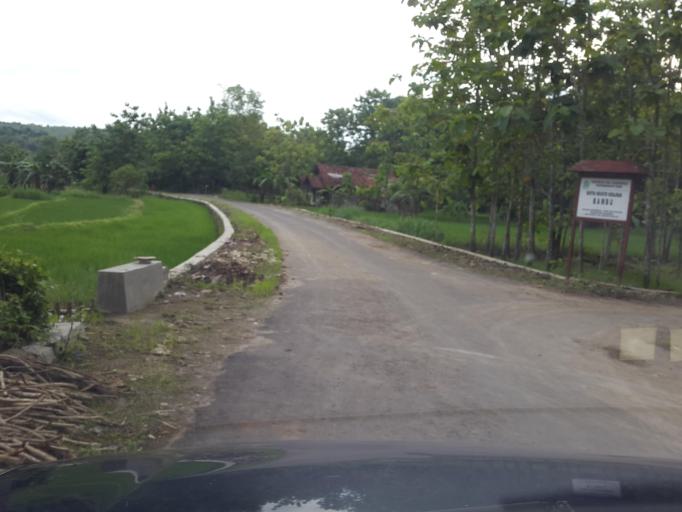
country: ID
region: Daerah Istimewa Yogyakarta
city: Wonosari
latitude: -7.8624
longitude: 110.6708
